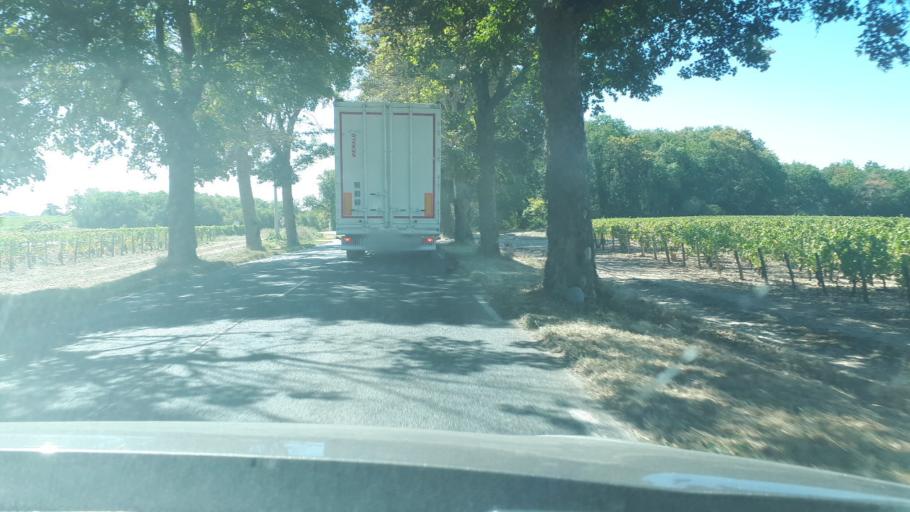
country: FR
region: Centre
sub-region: Departement du Cher
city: Sancerre
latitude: 47.3137
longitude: 2.8108
